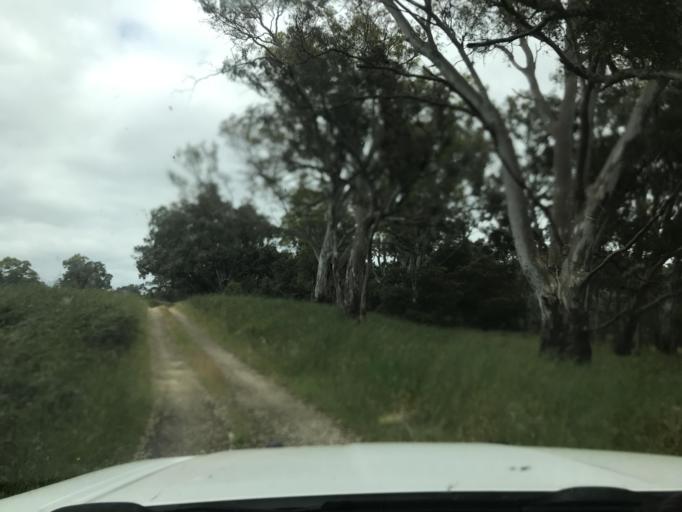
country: AU
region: South Australia
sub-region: Wattle Range
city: Penola
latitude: -37.1940
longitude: 140.9718
